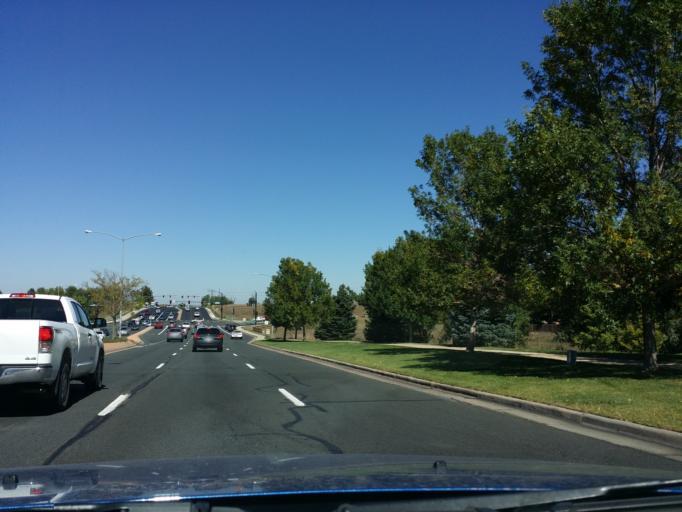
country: US
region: Colorado
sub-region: Adams County
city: Westminster
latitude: 39.8834
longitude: -105.0530
